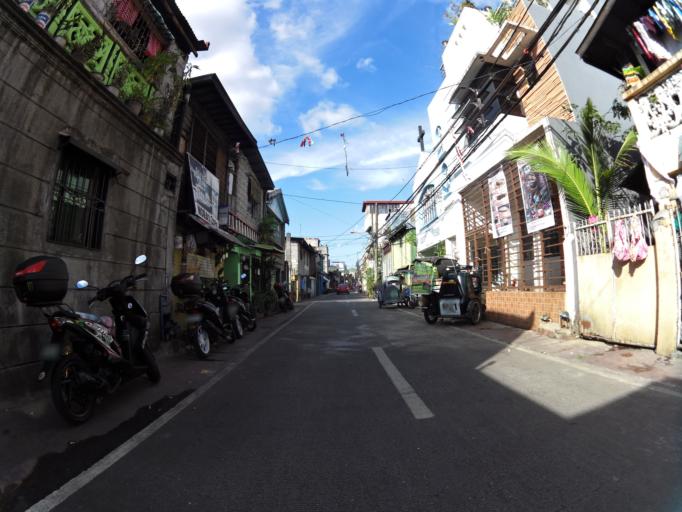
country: PH
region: Metro Manila
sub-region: Marikina
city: Calumpang
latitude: 14.6386
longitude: 121.0976
